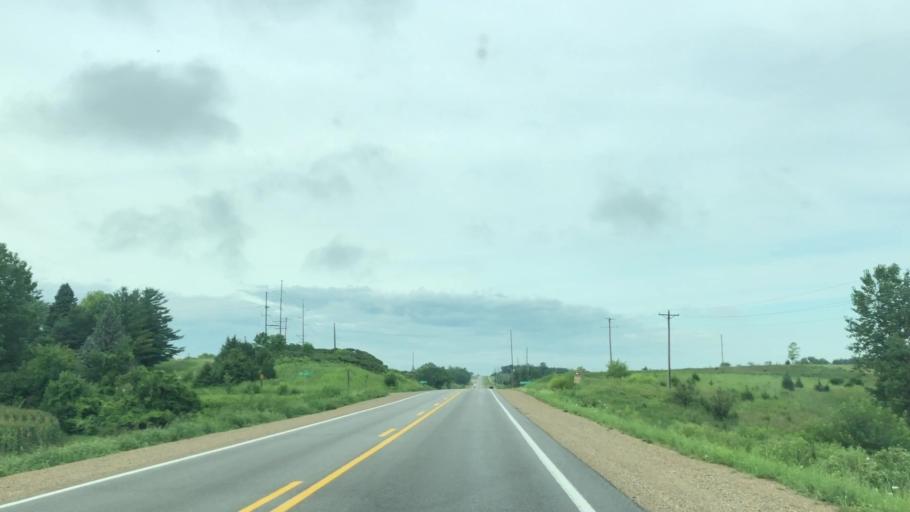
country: US
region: Iowa
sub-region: Marshall County
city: Marshalltown
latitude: 42.0075
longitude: -92.9578
